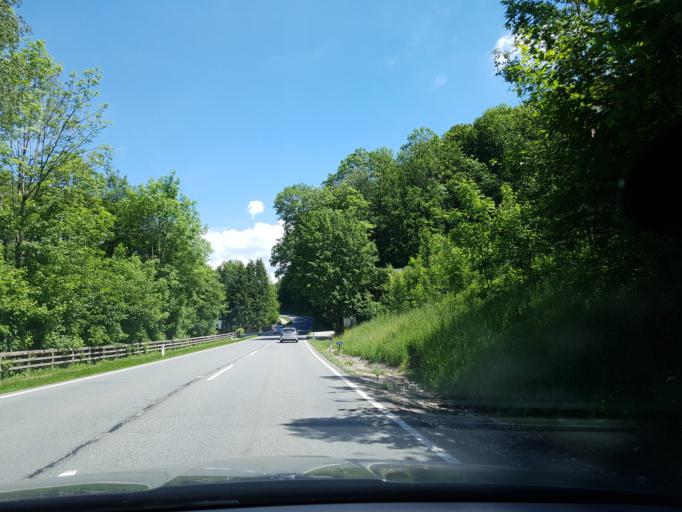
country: AT
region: Salzburg
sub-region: Politischer Bezirk Salzburg-Umgebung
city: Mattsee
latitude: 47.9582
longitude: 13.0918
